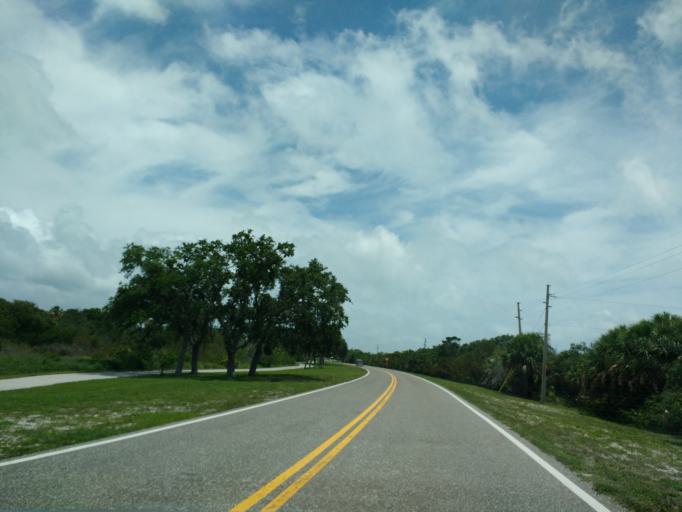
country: US
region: Florida
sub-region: Pinellas County
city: Tierra Verde
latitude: 27.6306
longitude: -82.7180
